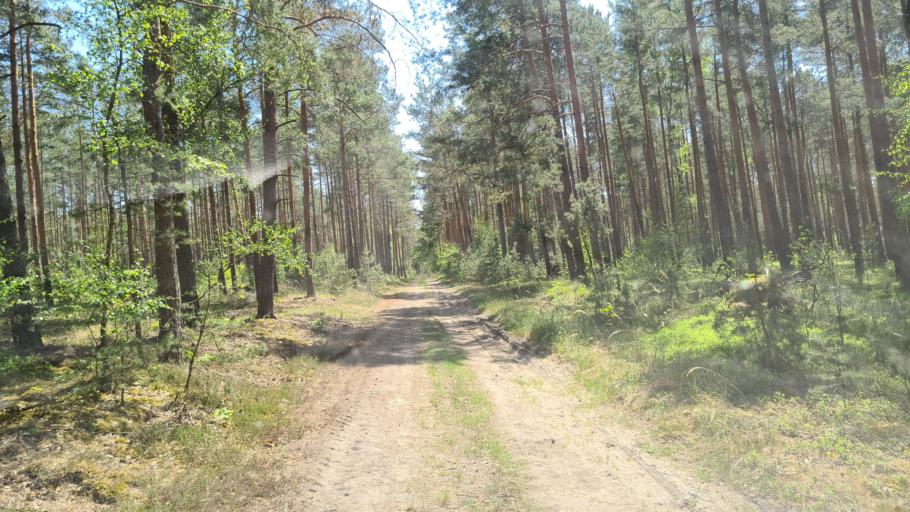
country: DE
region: Brandenburg
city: Sallgast
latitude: 51.5875
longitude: 13.8753
